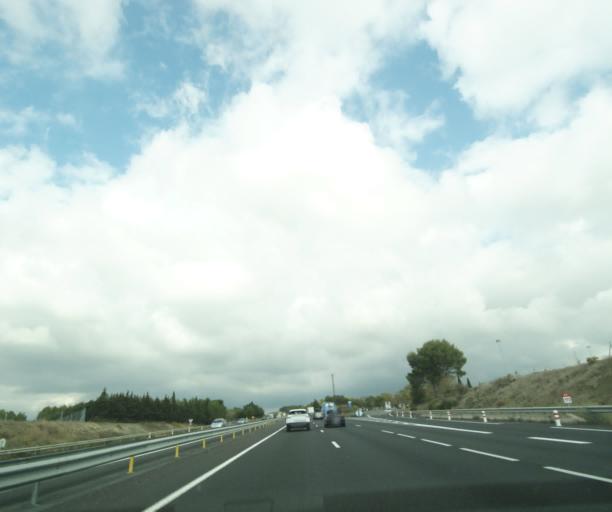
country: FR
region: Languedoc-Roussillon
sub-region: Departement de l'Herault
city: Lespignan
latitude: 43.2630
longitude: 3.1725
